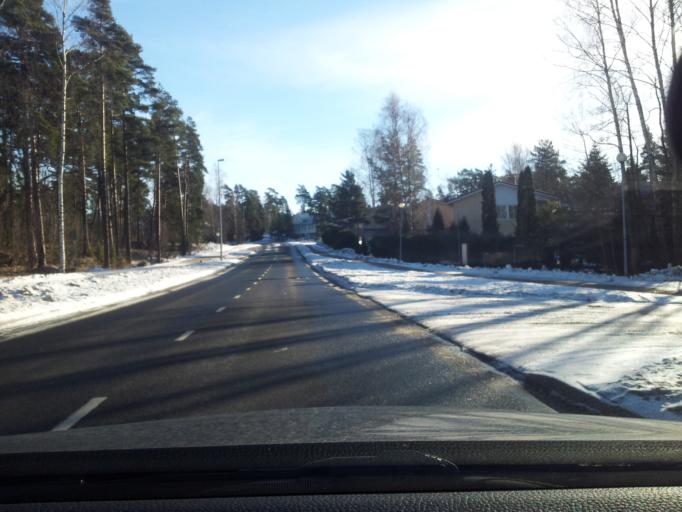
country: FI
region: Uusimaa
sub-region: Helsinki
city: Koukkuniemi
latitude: 60.1485
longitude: 24.7394
